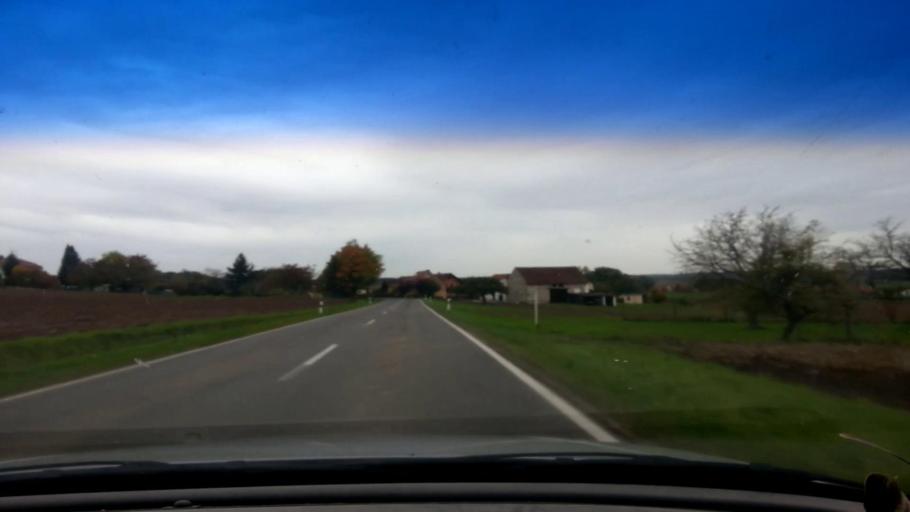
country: DE
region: Bavaria
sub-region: Upper Franconia
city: Priesendorf
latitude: 49.9037
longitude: 10.6813
